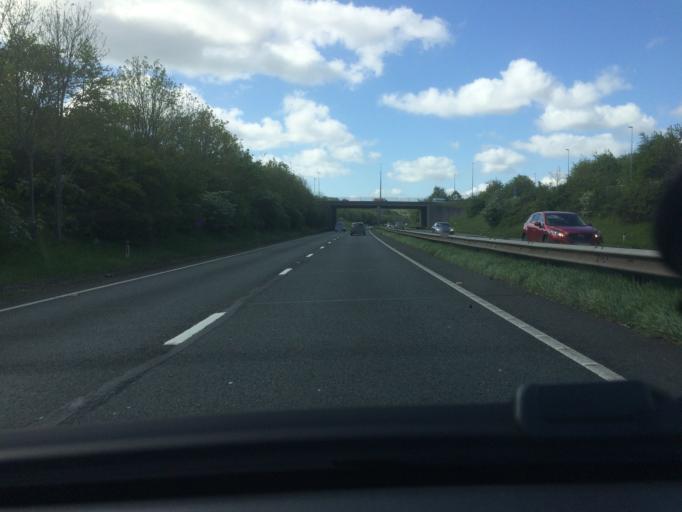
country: GB
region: Wales
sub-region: Wrexham
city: Rossett
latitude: 53.1070
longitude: -2.9563
